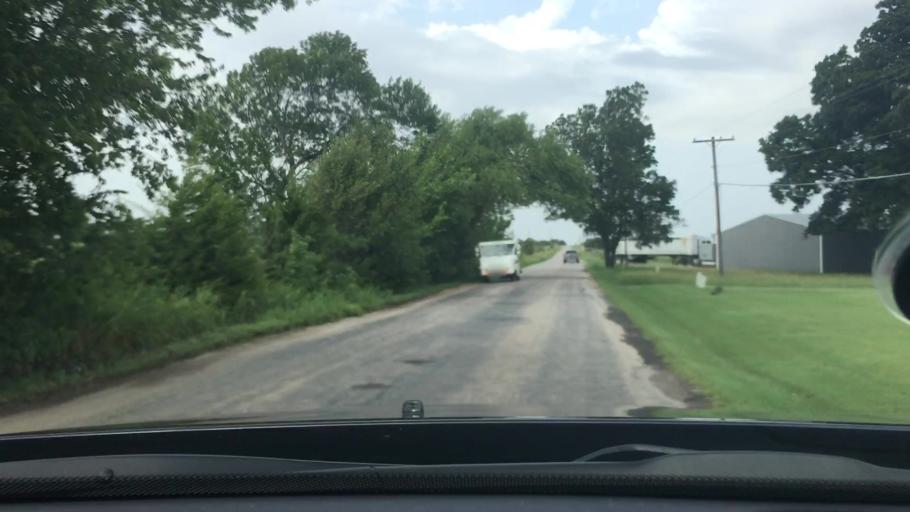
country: US
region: Oklahoma
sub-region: Carter County
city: Lone Grove
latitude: 34.2020
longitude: -97.2525
